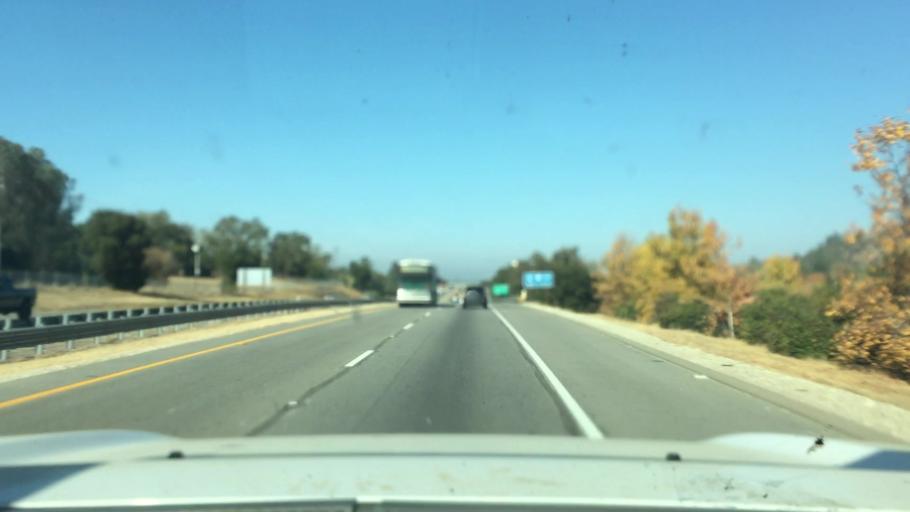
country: US
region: California
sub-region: San Luis Obispo County
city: Atascadero
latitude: 35.4573
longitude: -120.6444
